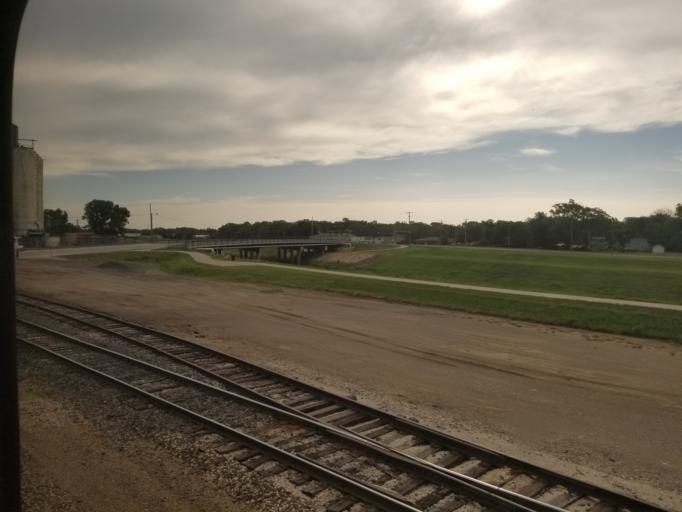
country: US
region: Kansas
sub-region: Shawnee County
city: Topeka
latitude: 39.0431
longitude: -95.6682
